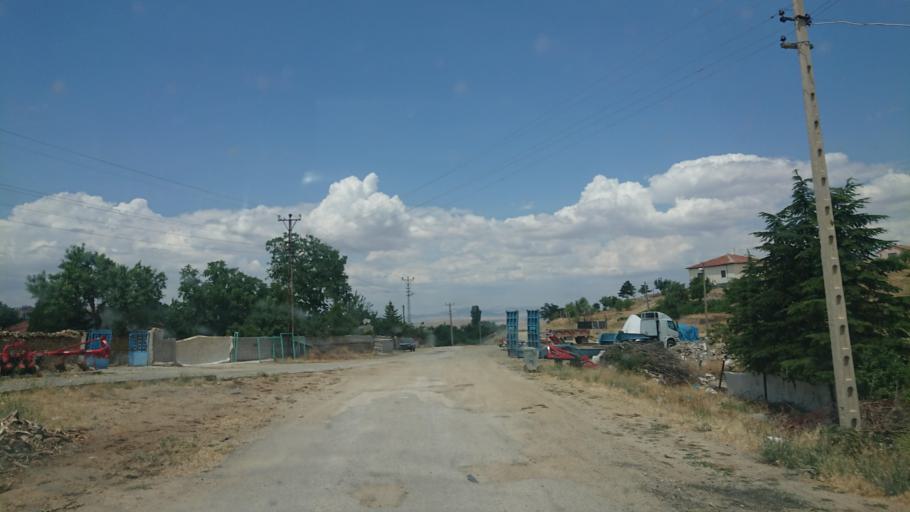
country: TR
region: Aksaray
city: Sariyahsi
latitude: 38.9560
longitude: 33.8831
